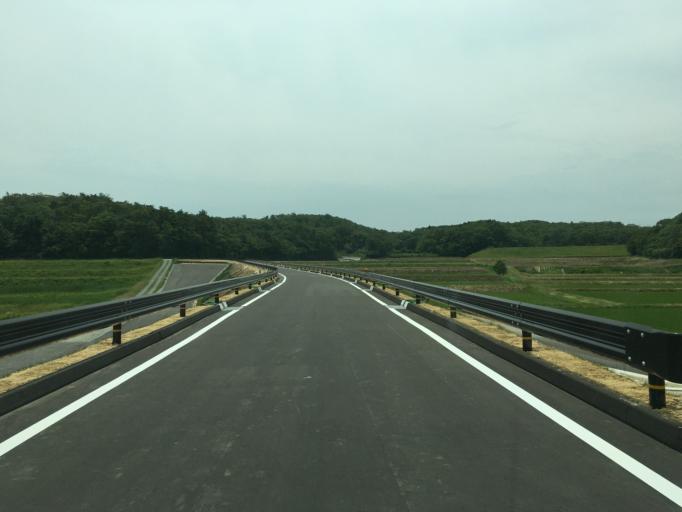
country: JP
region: Miyagi
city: Marumori
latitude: 37.7606
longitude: 140.9732
